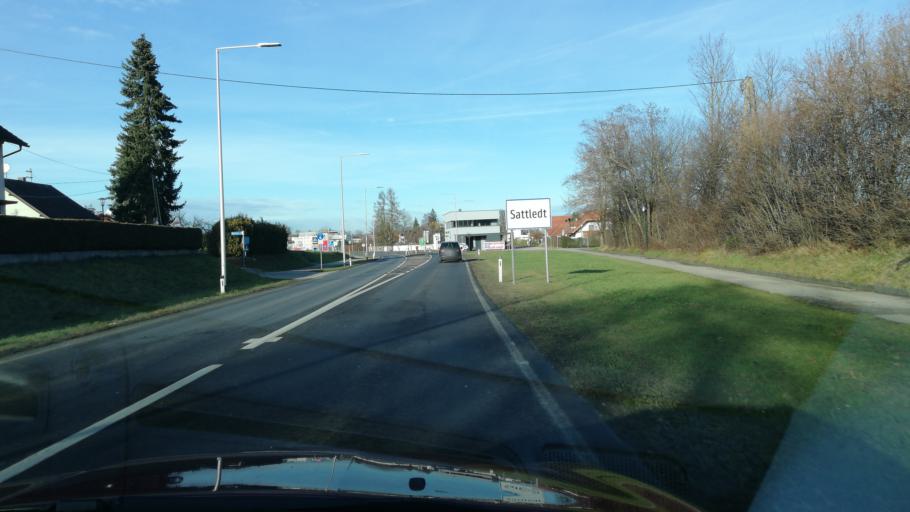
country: AT
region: Upper Austria
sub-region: Wels-Land
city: Sattledt
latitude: 48.0681
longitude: 14.0544
